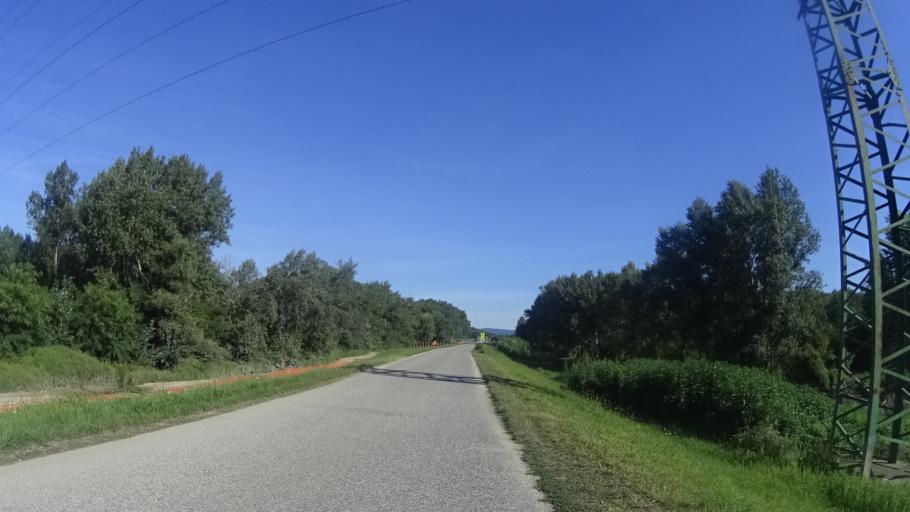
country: SK
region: Bratislavsky
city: Bratislava
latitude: 48.1006
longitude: 17.1485
